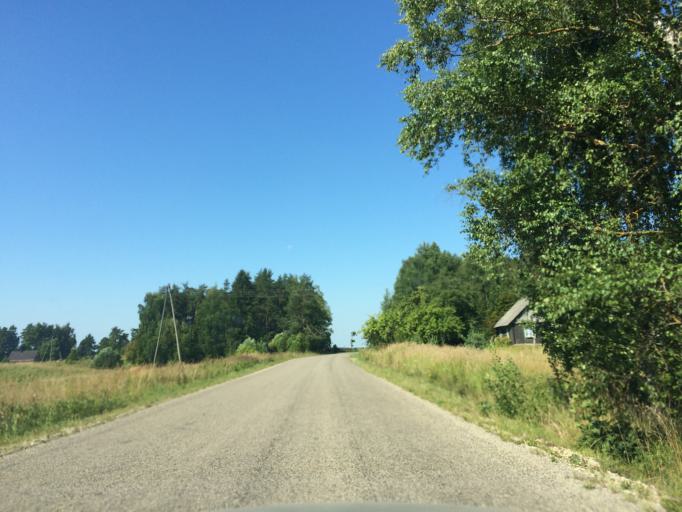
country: LV
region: Rezekne
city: Rezekne
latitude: 56.4883
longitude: 27.2430
